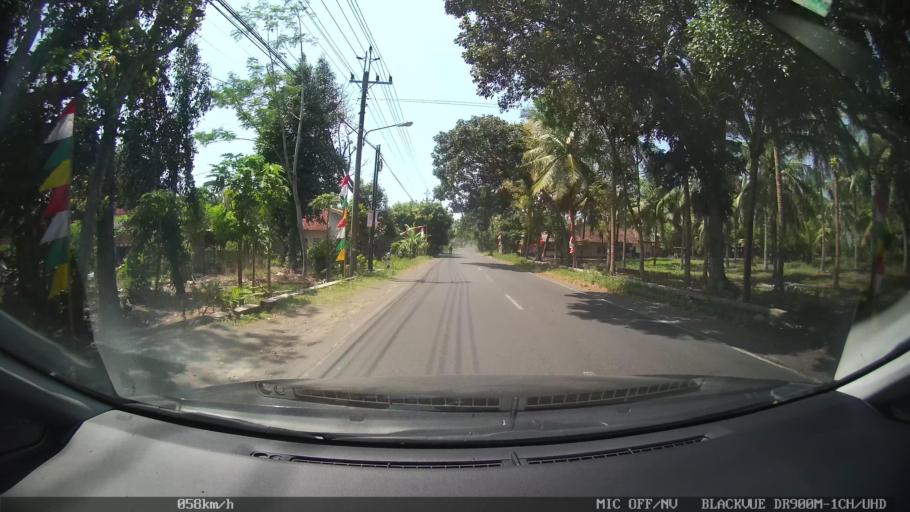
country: ID
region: Daerah Istimewa Yogyakarta
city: Srandakan
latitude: -7.9115
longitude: 110.0901
